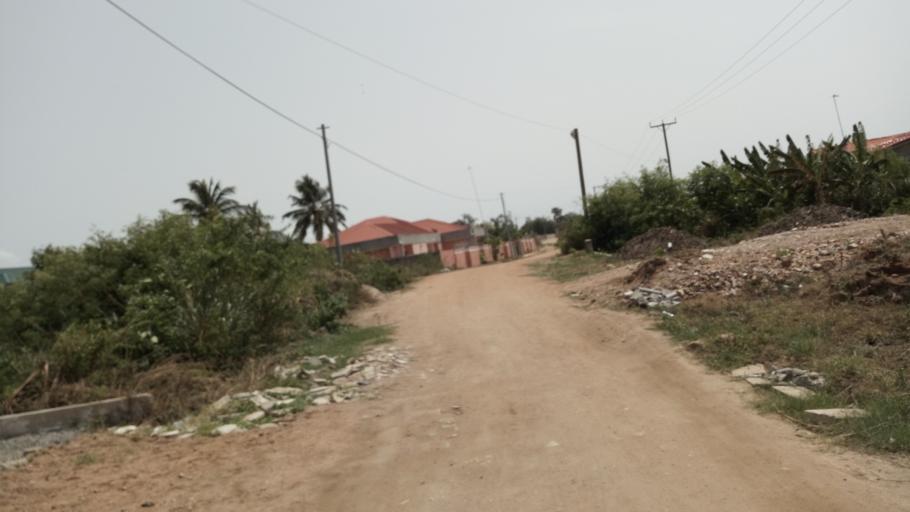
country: GH
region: Central
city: Winneba
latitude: 5.3649
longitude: -0.6408
